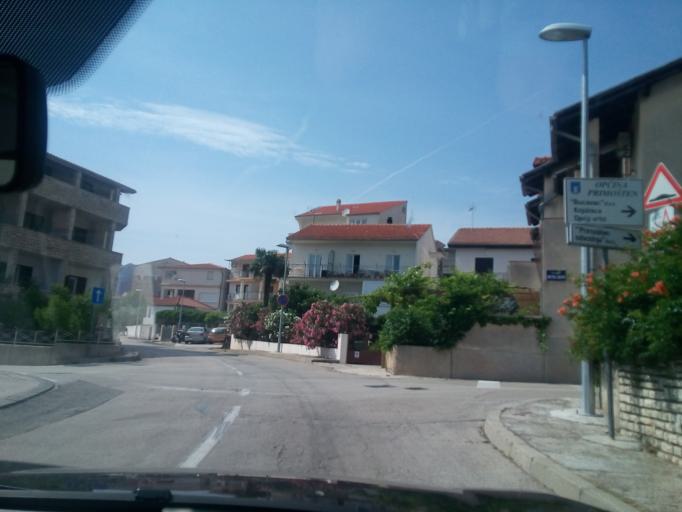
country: HR
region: Sibensko-Kniniska
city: Primosten
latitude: 43.5865
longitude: 15.9279
